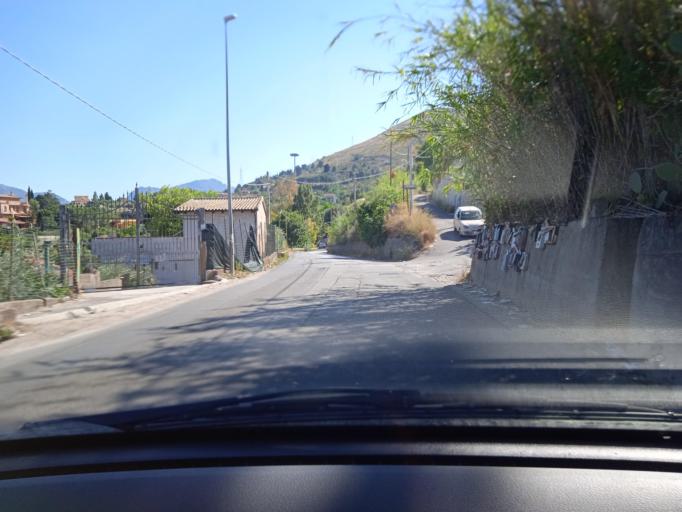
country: IT
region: Sicily
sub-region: Palermo
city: Cannizzaro-Favara
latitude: 38.0717
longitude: 13.2705
